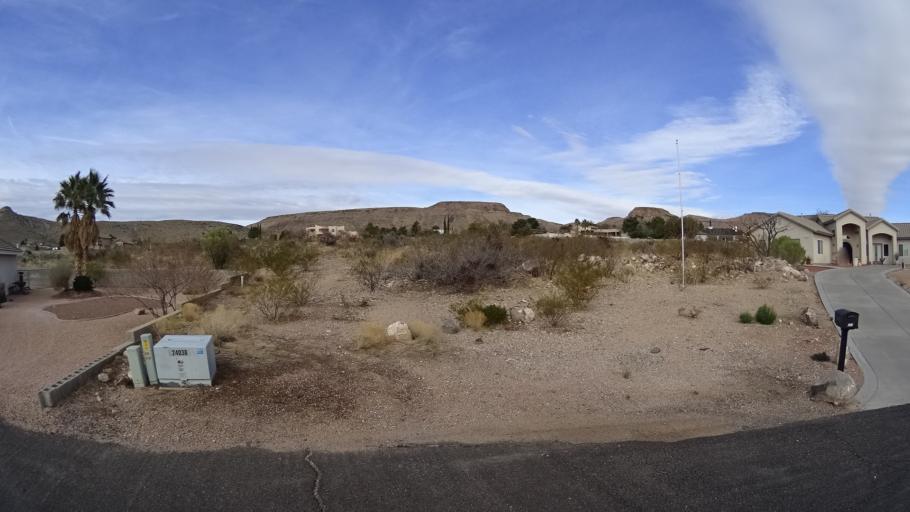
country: US
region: Arizona
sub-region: Mohave County
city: New Kingman-Butler
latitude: 35.2341
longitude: -114.0505
